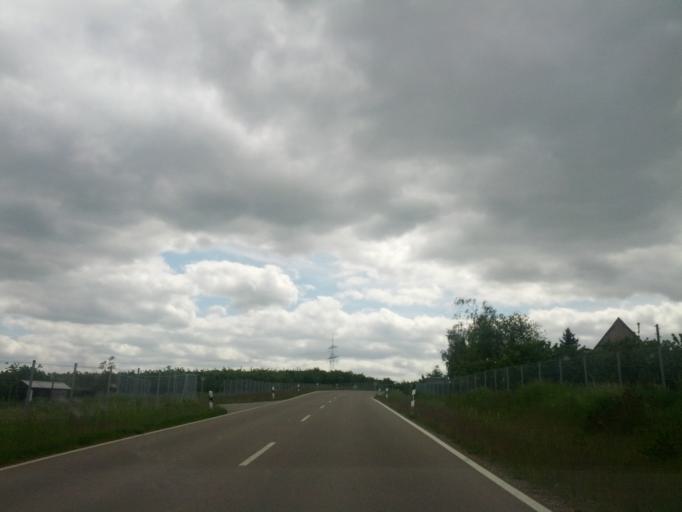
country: DE
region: Saxony
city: Kreischa
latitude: 50.9556
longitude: 13.7950
